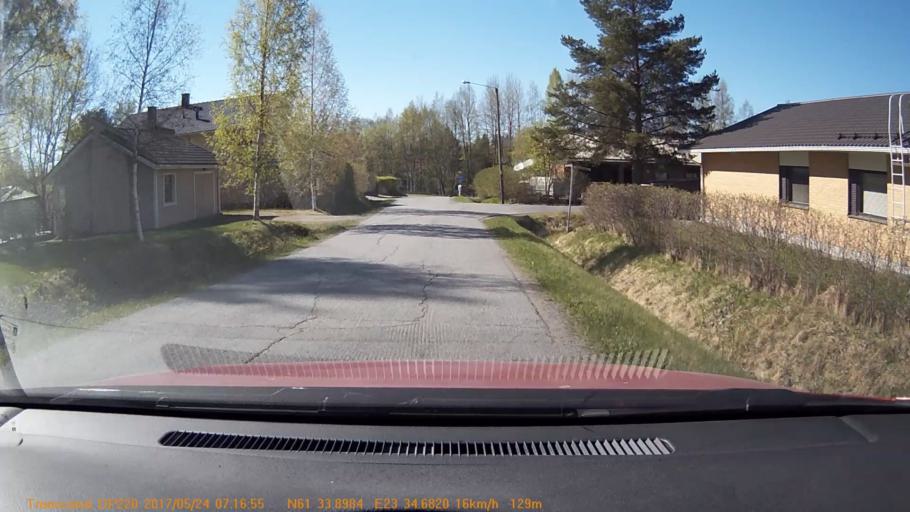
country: FI
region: Pirkanmaa
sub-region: Tampere
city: Yloejaervi
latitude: 61.5650
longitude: 23.5780
